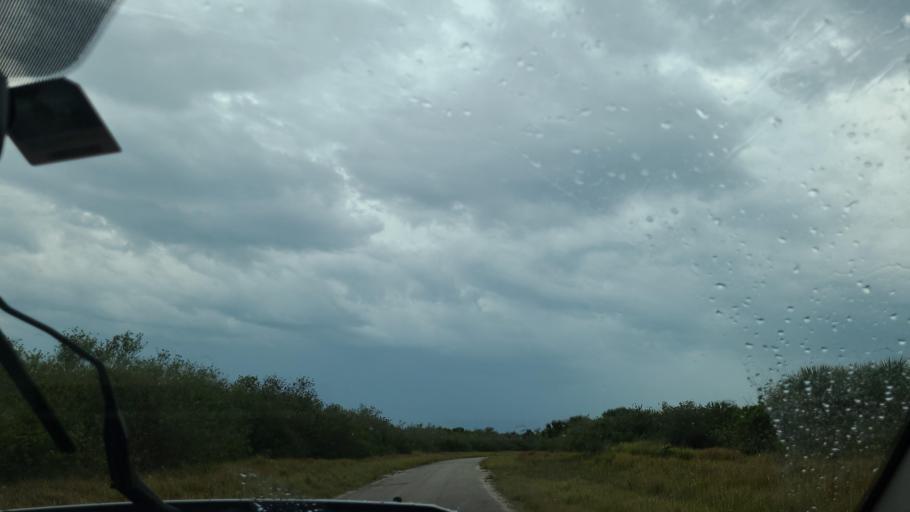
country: US
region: Florida
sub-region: Brevard County
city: June Park
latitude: 27.9469
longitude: -80.7106
